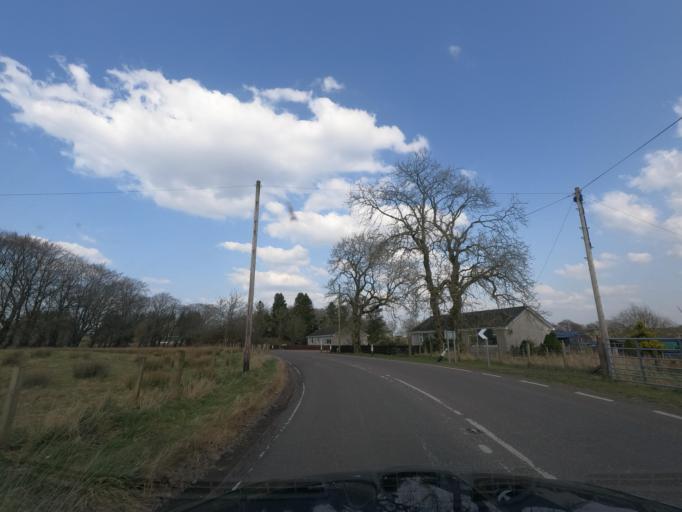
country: GB
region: Scotland
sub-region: South Lanarkshire
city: Forth
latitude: 55.7611
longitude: -3.6677
